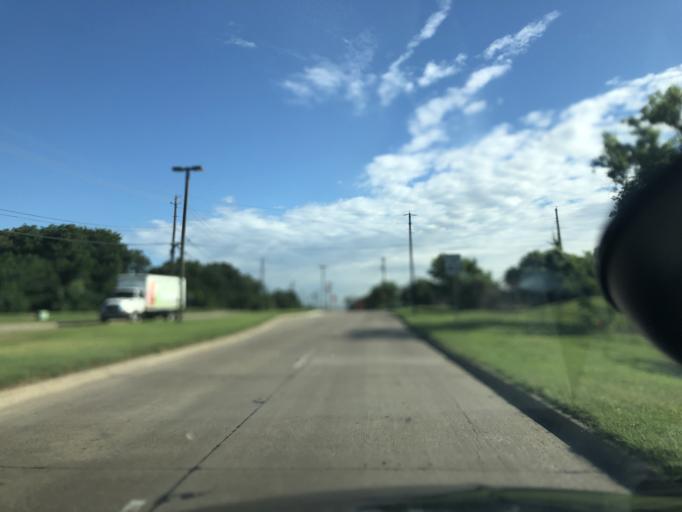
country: US
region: Texas
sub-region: Tarrant County
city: Euless
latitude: 32.8172
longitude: -97.0304
